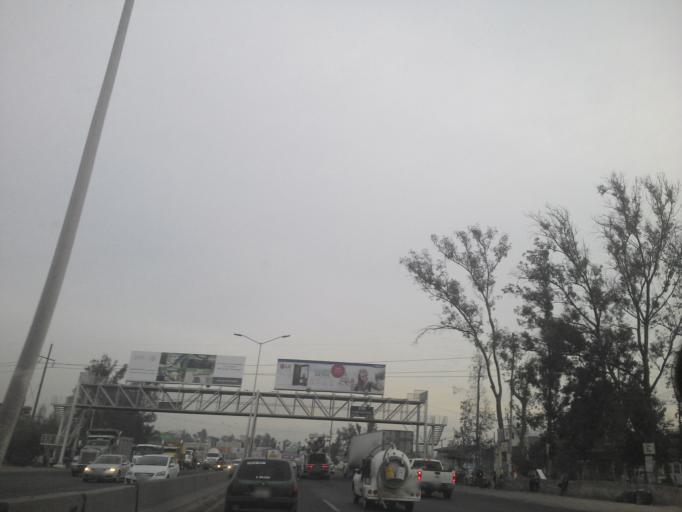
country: MX
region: Jalisco
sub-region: Tlajomulco de Zuniga
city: La Tijera
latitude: 20.6130
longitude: -103.4241
